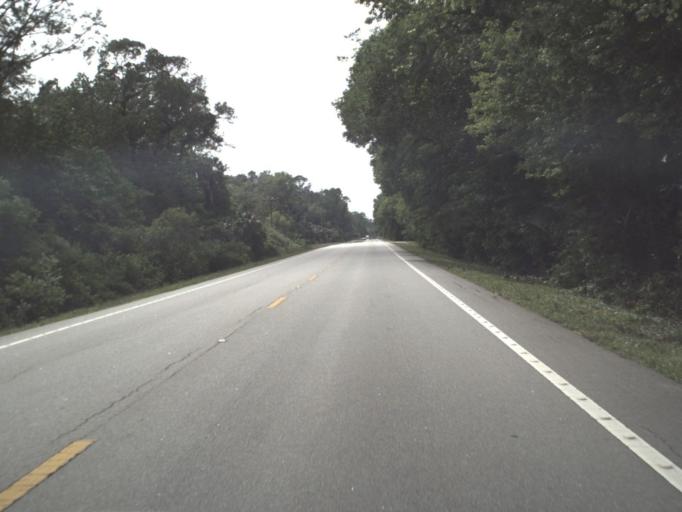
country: US
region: Florida
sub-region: Flagler County
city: Bunnell
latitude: 29.4679
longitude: -81.3045
